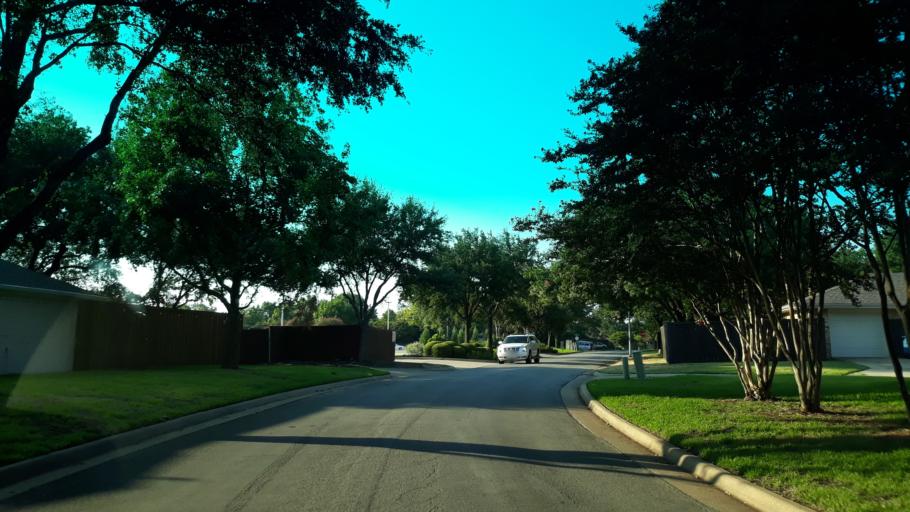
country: US
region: Texas
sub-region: Dallas County
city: Addison
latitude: 32.9485
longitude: -96.7956
